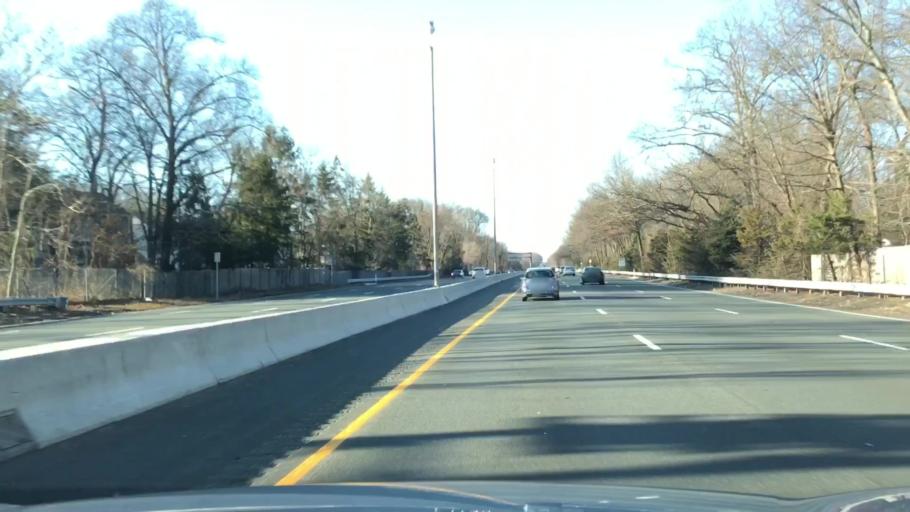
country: US
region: New Jersey
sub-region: Bergen County
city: Wyckoff
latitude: 40.9873
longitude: -74.1680
